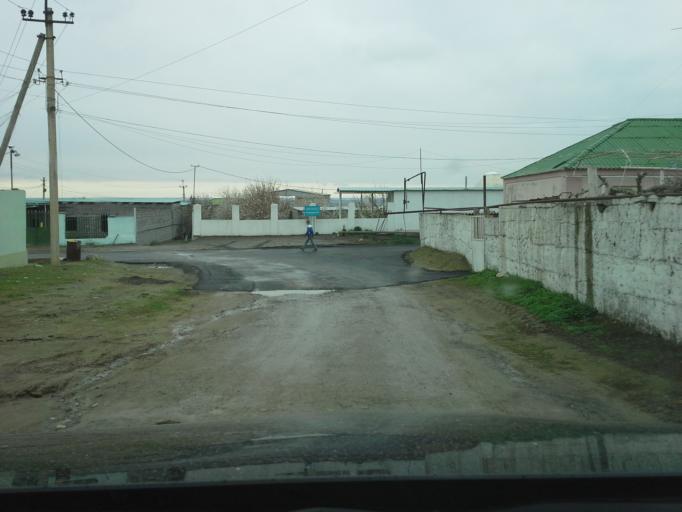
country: TM
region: Ahal
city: Abadan
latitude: 37.9595
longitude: 58.2030
